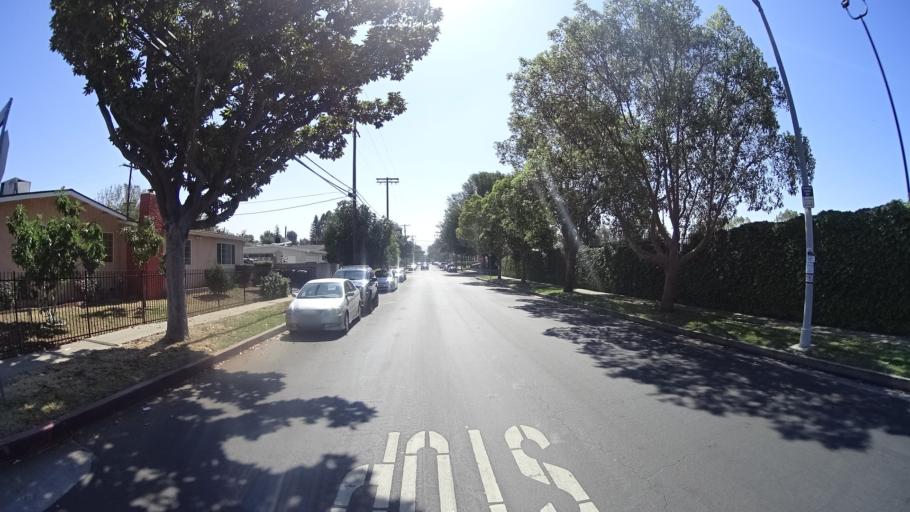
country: US
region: California
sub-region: Los Angeles County
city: Van Nuys
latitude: 34.2226
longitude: -118.4374
